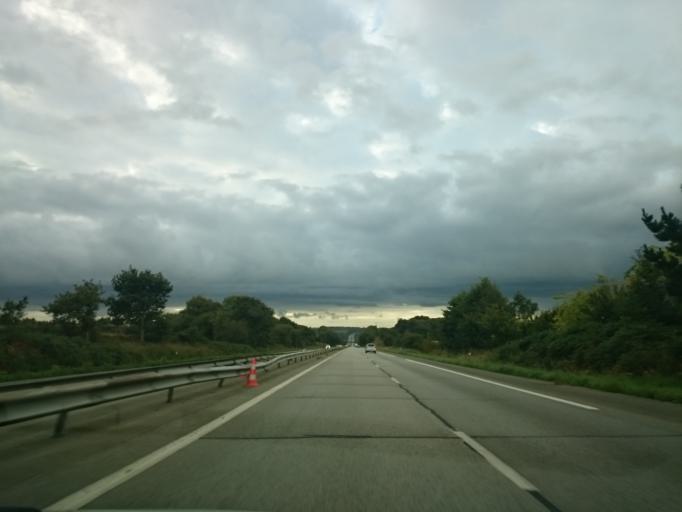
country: FR
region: Brittany
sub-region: Departement du Finistere
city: Briec
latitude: 48.1488
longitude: -4.0347
